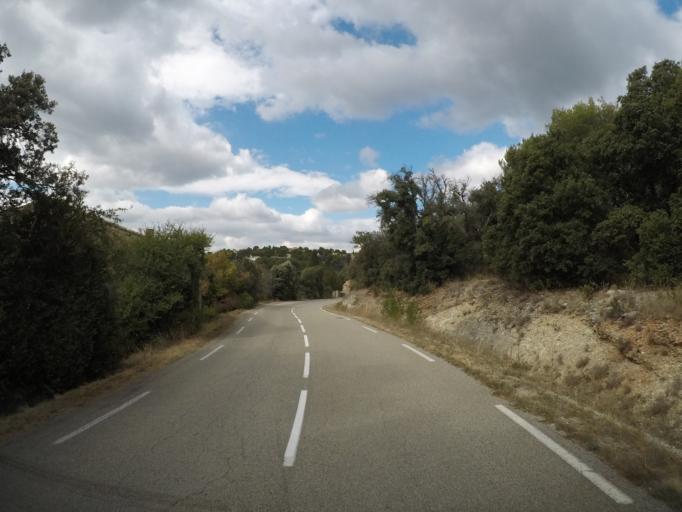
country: FR
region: Rhone-Alpes
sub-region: Departement de la Drome
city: Buis-les-Baronnies
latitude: 44.2271
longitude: 5.2002
